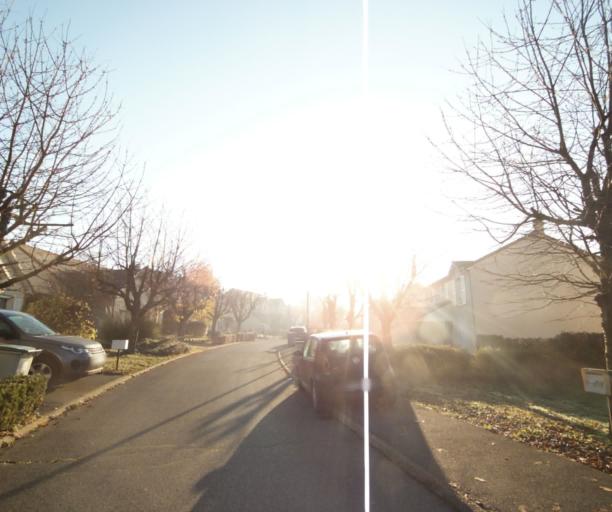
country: FR
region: Ile-de-France
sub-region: Departement du Val-d'Oise
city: Gonesse
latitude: 48.9965
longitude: 2.4328
